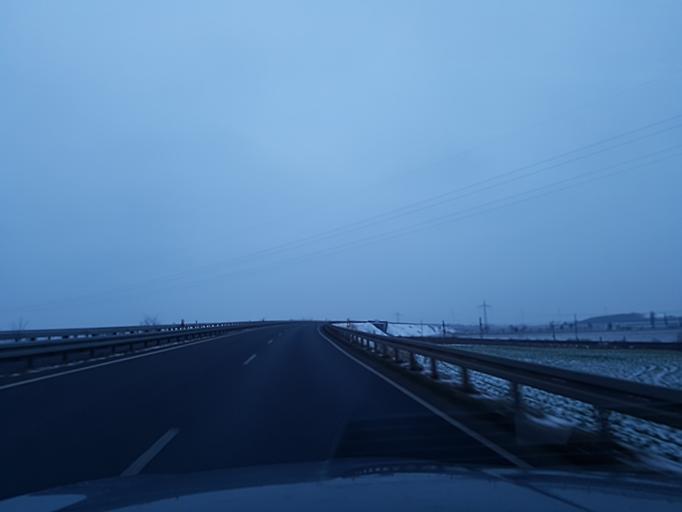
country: DE
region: Saxony
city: Riesa
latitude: 51.2902
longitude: 13.2753
